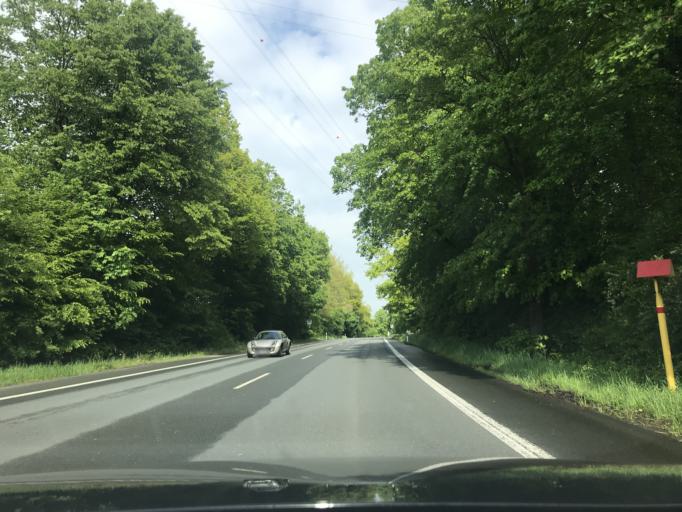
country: DE
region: North Rhine-Westphalia
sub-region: Regierungsbezirk Arnsberg
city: Hagen
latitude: 51.4113
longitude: 7.4963
